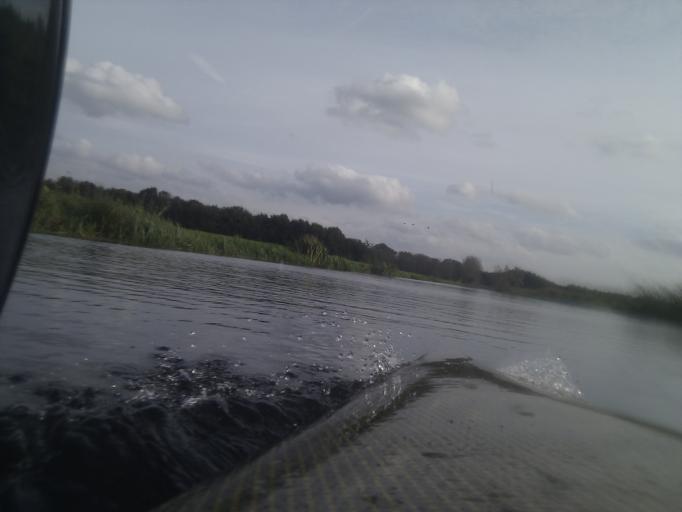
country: NL
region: Utrecht
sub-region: Gemeente De Bilt
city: De Bilt
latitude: 52.0978
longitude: 5.1928
